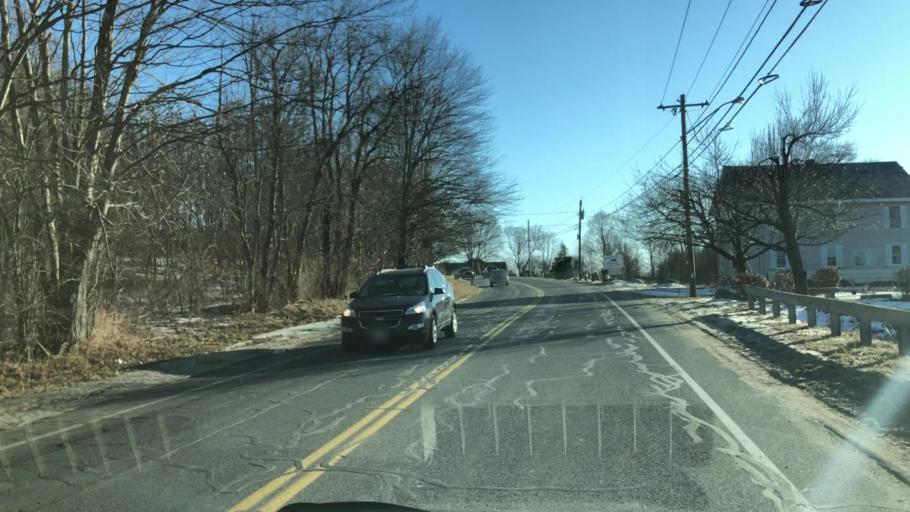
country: US
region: Massachusetts
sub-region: Hampshire County
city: Easthampton
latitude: 42.2953
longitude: -72.6730
